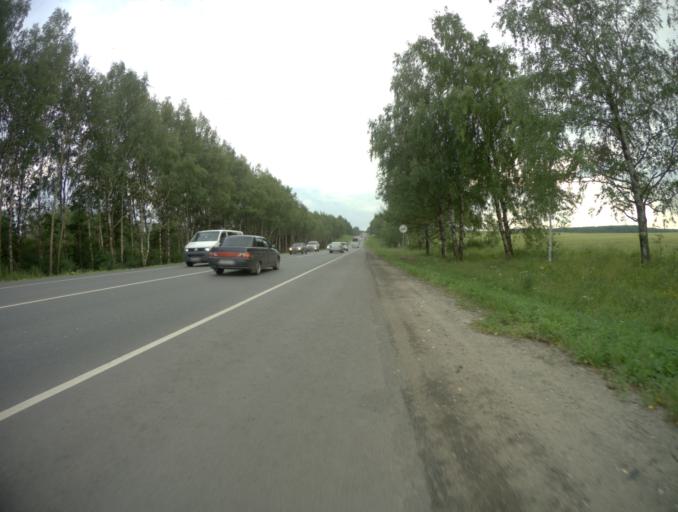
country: RU
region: Vladimir
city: Bogolyubovo
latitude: 56.2486
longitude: 40.4571
